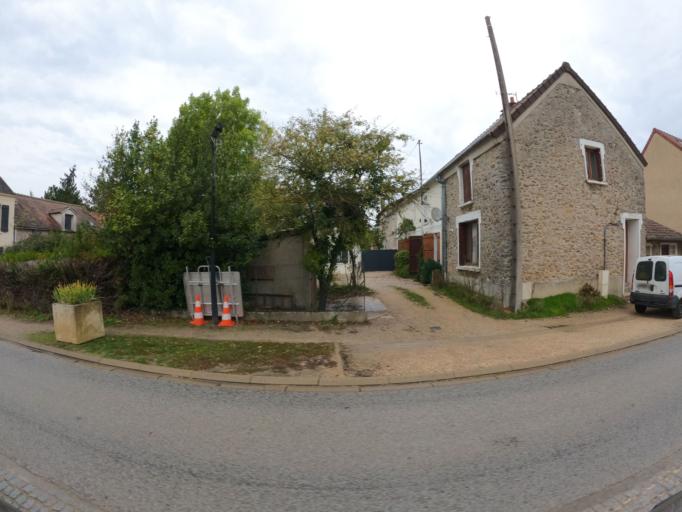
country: FR
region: Ile-de-France
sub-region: Departement de Seine-et-Marne
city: Serris
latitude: 48.8160
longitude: 2.7940
